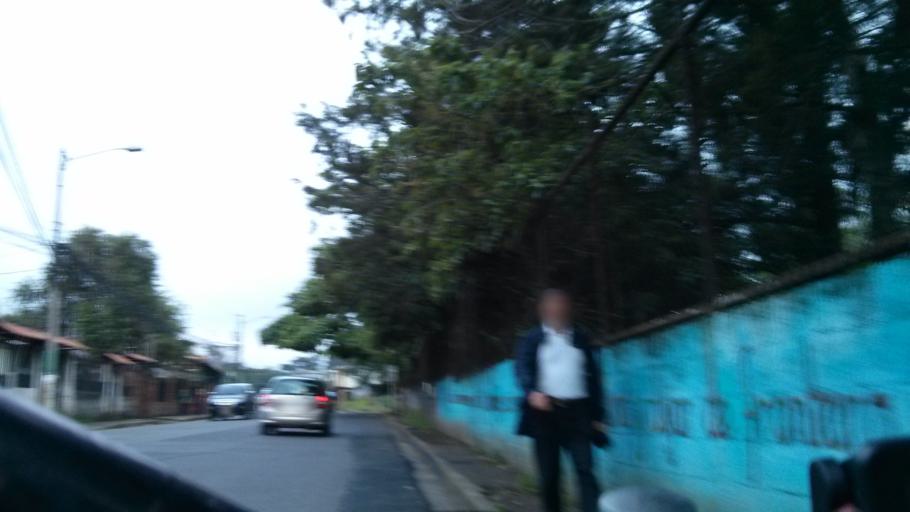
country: CR
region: San Jose
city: San Pedro
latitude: 9.9351
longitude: -84.0479
